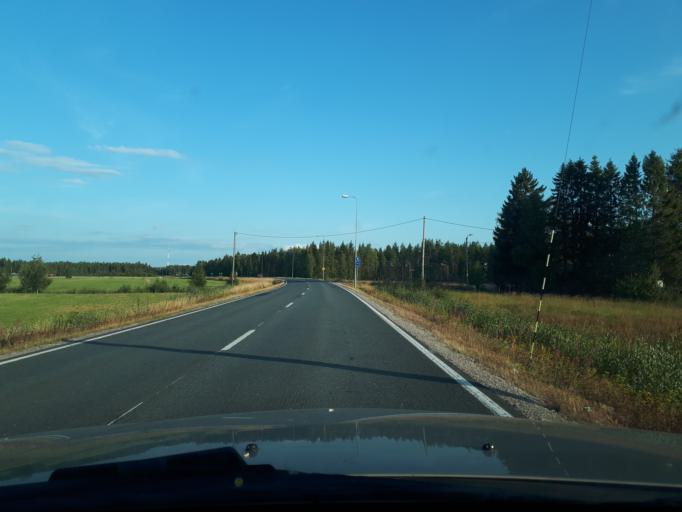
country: FI
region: Northern Ostrobothnia
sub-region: Oulu
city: Oulunsalo
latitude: 64.9812
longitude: 25.2722
